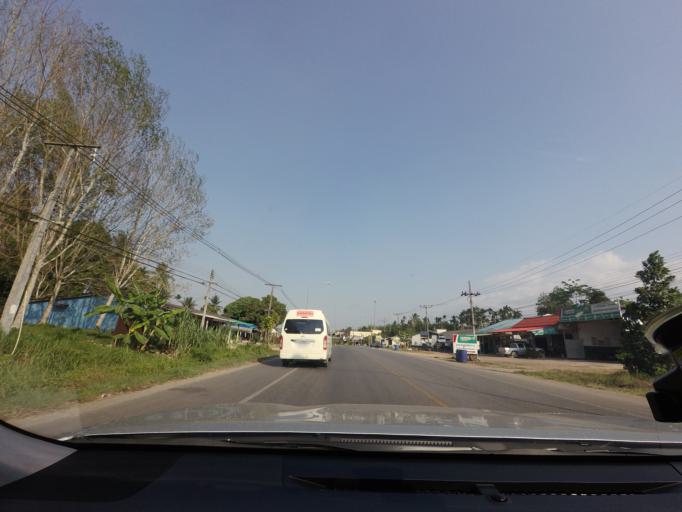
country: TH
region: Surat Thani
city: Phrasaeng
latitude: 8.5730
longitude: 99.2243
